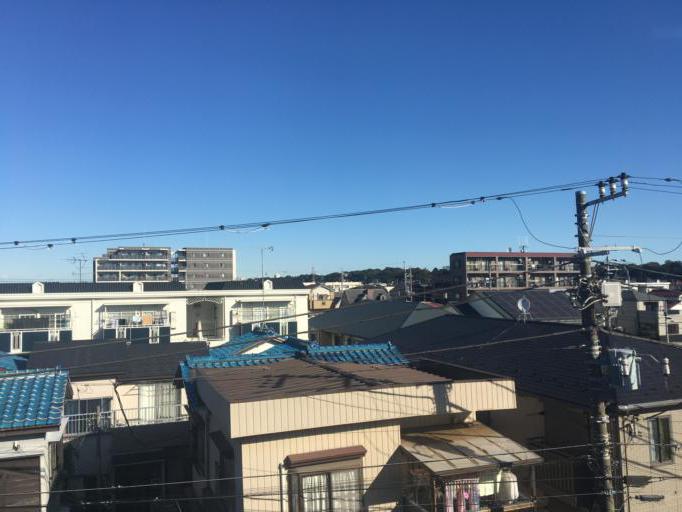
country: JP
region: Chiba
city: Matsudo
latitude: 35.7382
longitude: 139.8943
